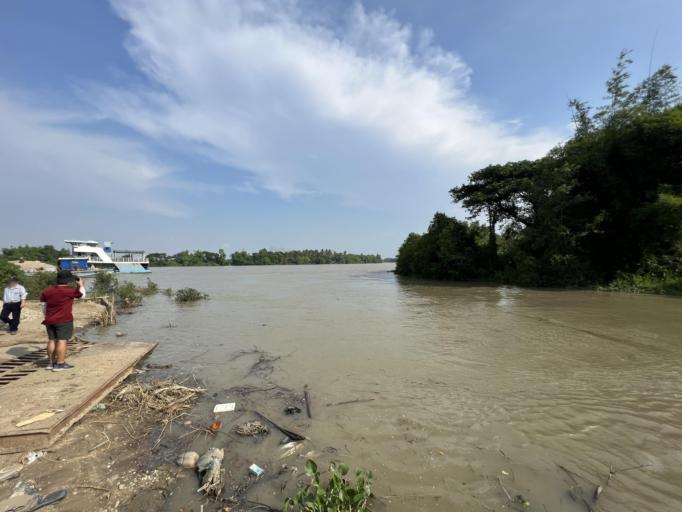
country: MM
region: Ayeyarwady
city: Kyaiklat
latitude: 16.4282
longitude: 95.7298
